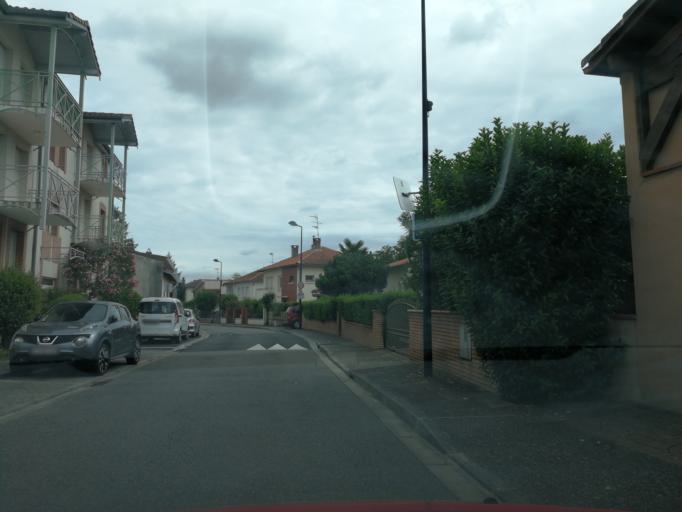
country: FR
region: Midi-Pyrenees
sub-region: Departement de la Haute-Garonne
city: Auzeville-Tolosane
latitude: 43.5307
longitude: 1.4785
